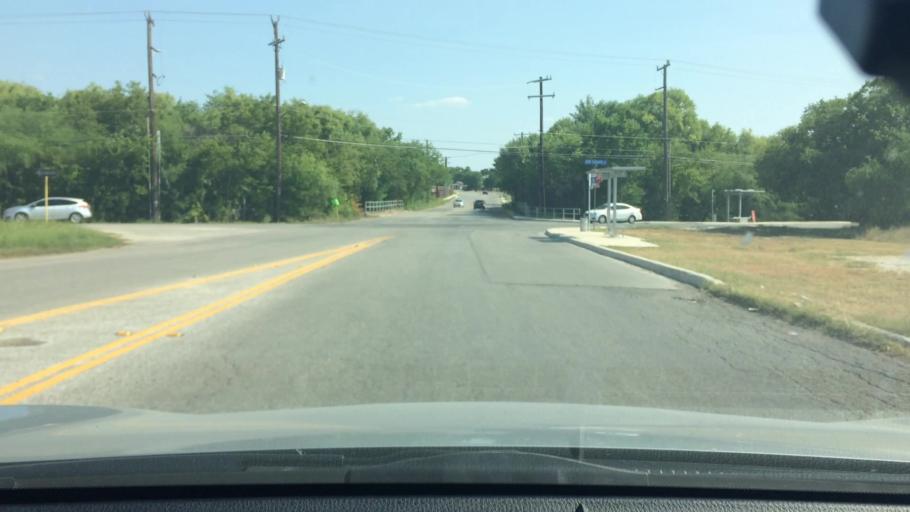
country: US
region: Texas
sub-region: Bexar County
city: Kirby
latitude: 29.4746
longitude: -98.3753
